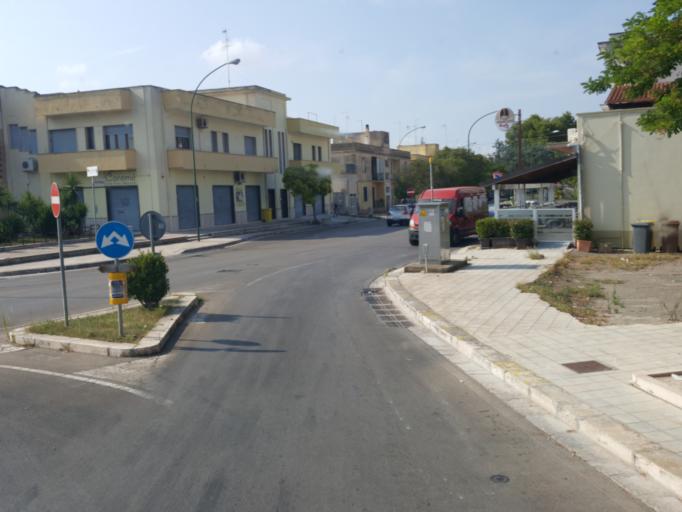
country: IT
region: Apulia
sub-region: Provincia di Lecce
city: Campi Salentina
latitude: 40.4019
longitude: 18.0213
